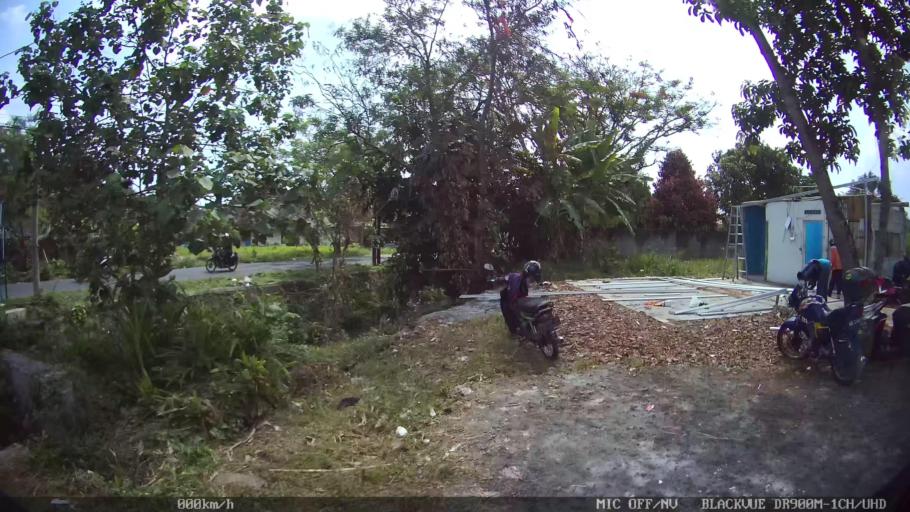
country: ID
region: Daerah Istimewa Yogyakarta
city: Kasihan
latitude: -7.8119
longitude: 110.3368
